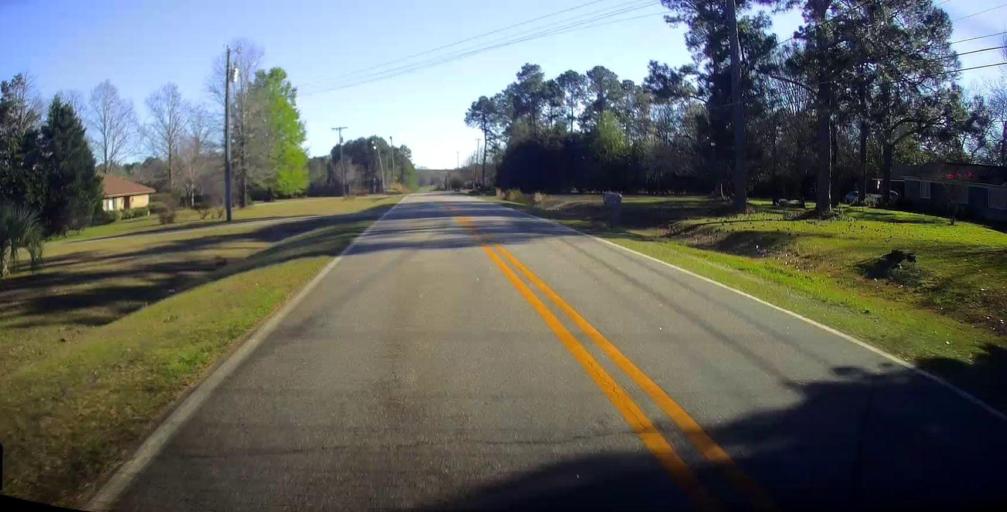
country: US
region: Georgia
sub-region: Peach County
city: Fort Valley
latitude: 32.5633
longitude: -83.9160
